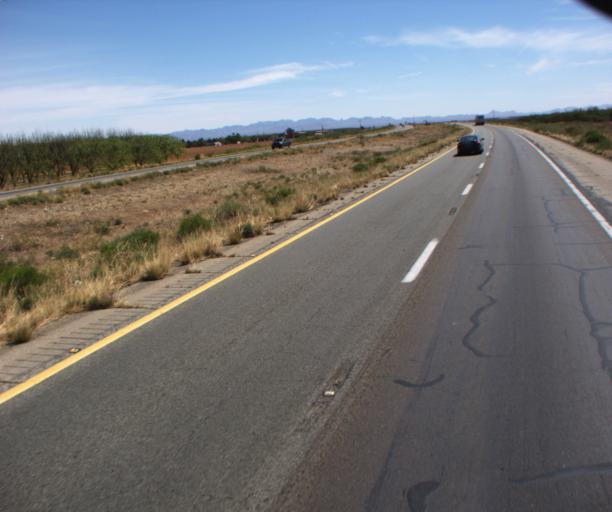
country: US
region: Arizona
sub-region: Cochise County
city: Willcox
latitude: 32.3177
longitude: -109.4909
